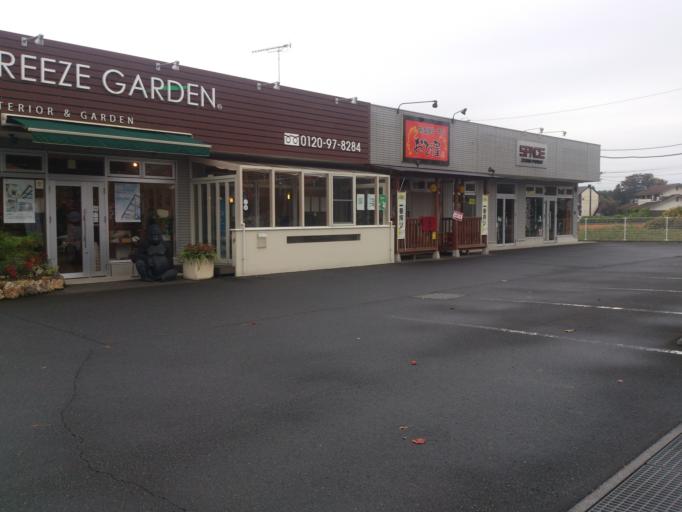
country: JP
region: Ibaraki
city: Tsukuba
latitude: 36.1033
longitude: 140.0845
